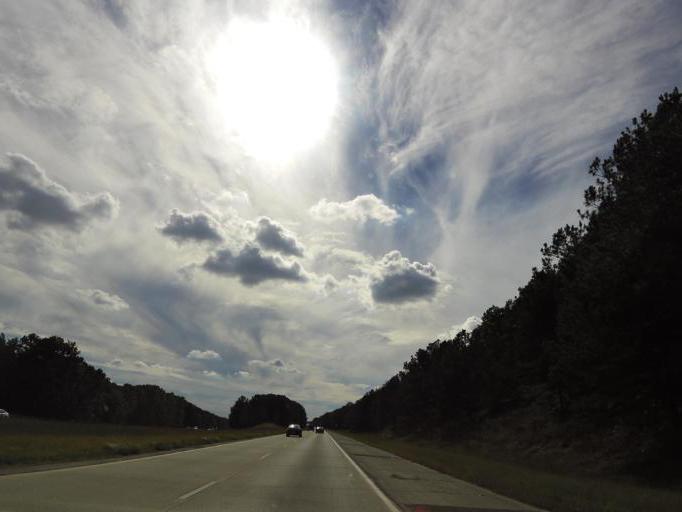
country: US
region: Georgia
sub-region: Cherokee County
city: Canton
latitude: 34.2875
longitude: -84.4437
